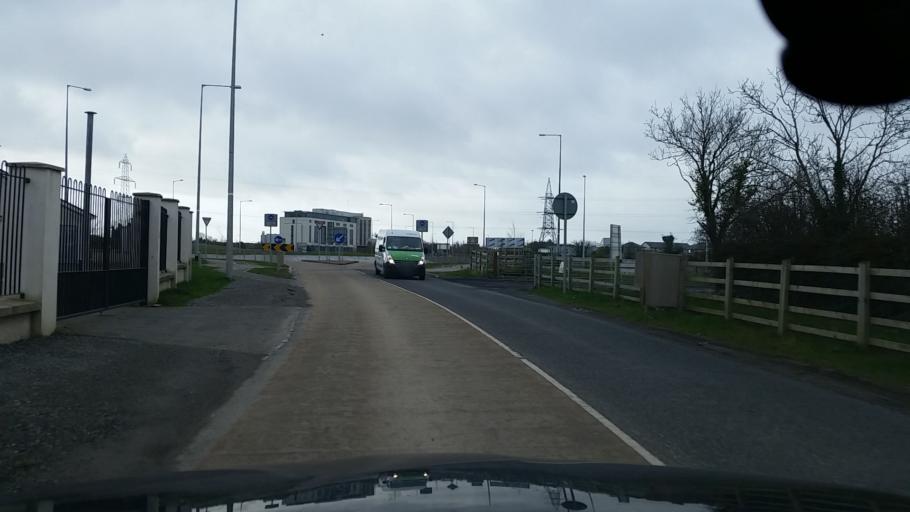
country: IE
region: Leinster
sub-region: Fingal County
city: Blanchardstown
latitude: 53.4235
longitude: -6.3786
